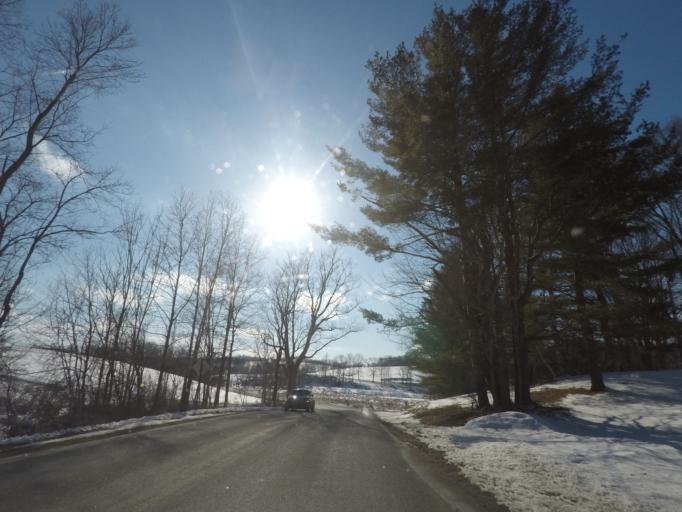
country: US
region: New York
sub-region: Rensselaer County
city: Hoosick Falls
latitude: 42.8832
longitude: -73.4968
